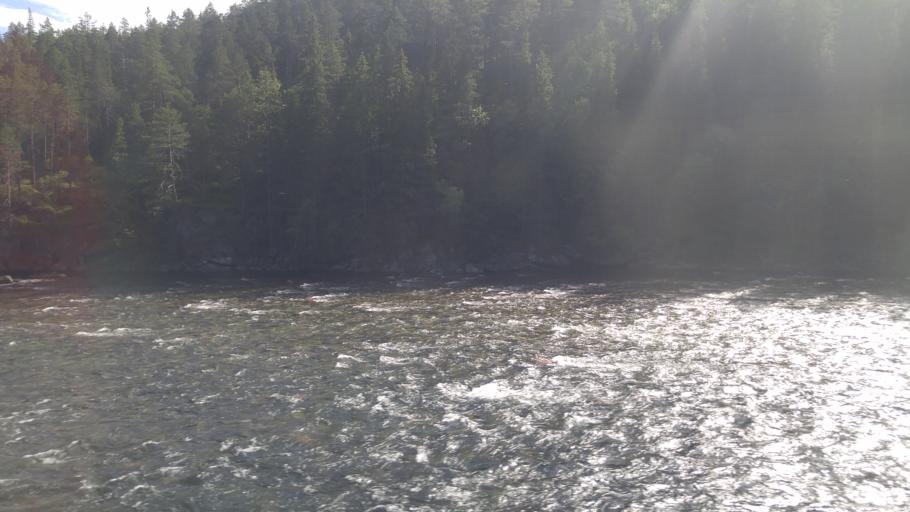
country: NO
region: Sor-Trondelag
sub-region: Selbu
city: Mebonden
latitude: 62.9650
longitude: 10.9660
